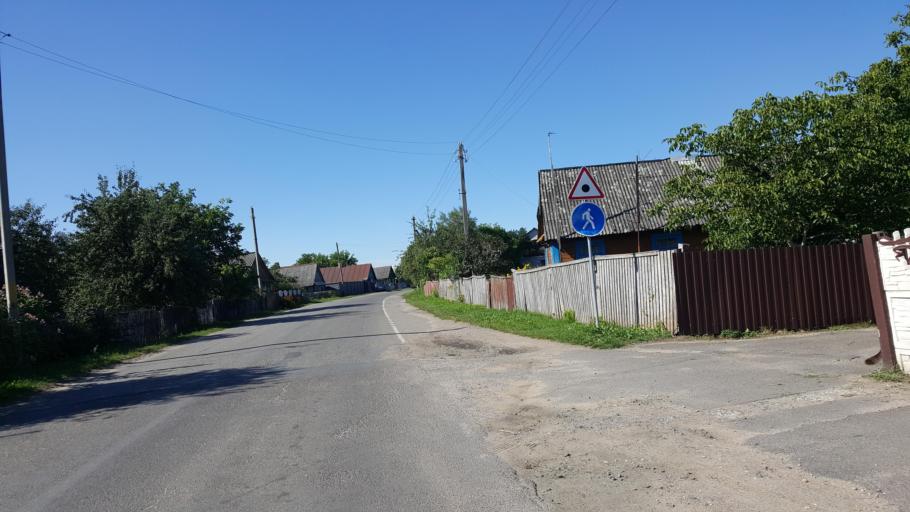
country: BY
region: Brest
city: Charnawchytsy
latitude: 52.2218
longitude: 23.7389
